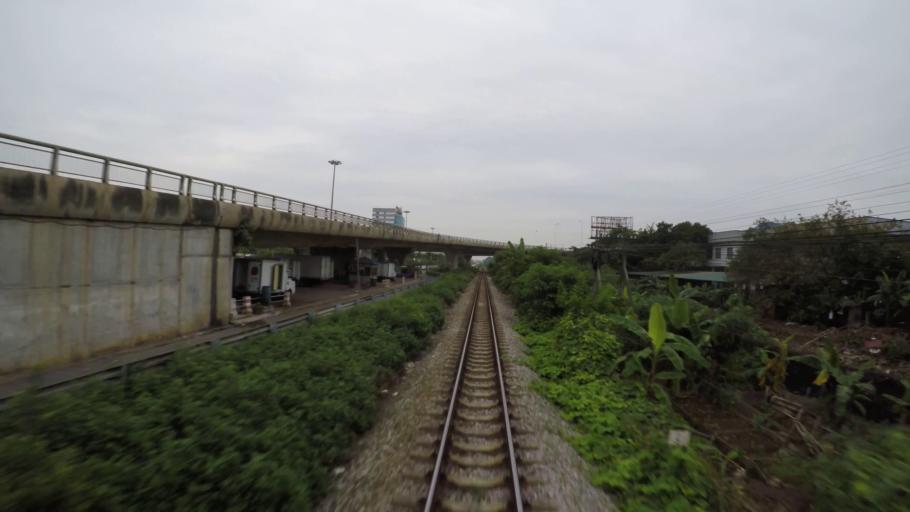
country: VN
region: Ha Noi
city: Trau Quy
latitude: 21.0075
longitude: 105.9569
